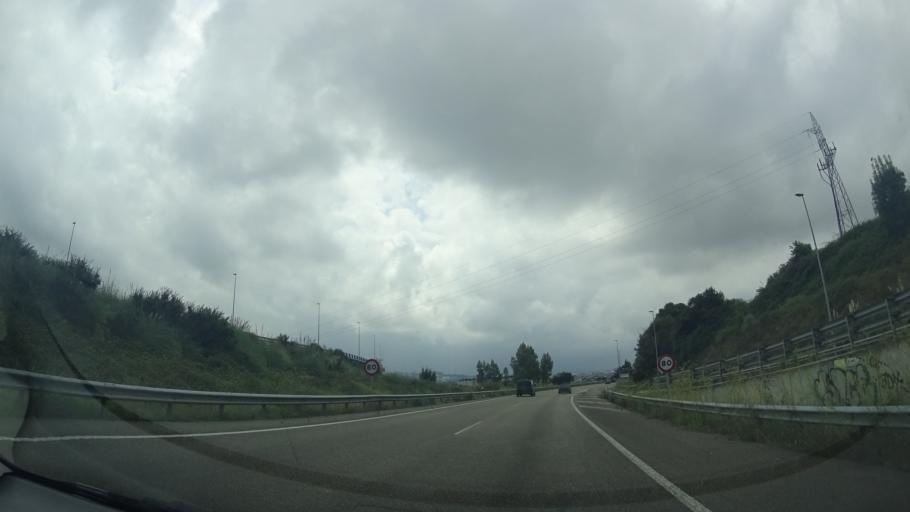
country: ES
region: Asturias
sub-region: Province of Asturias
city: Lugones
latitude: 43.3754
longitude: -5.8162
